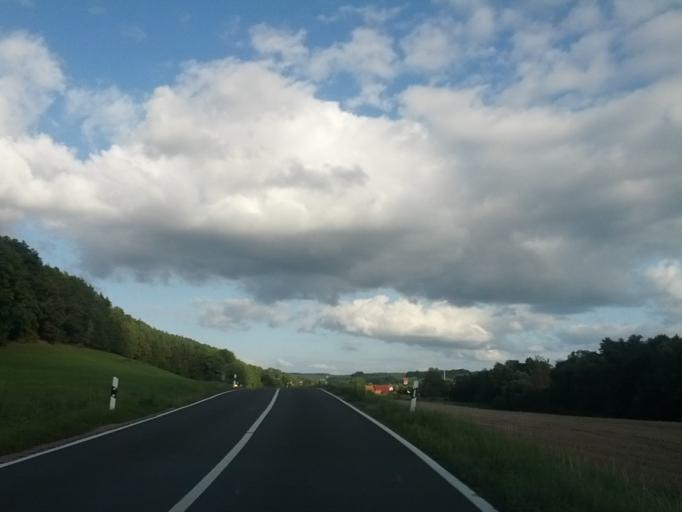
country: DE
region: Thuringia
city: Marksuhl
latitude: 50.9417
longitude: 10.2220
